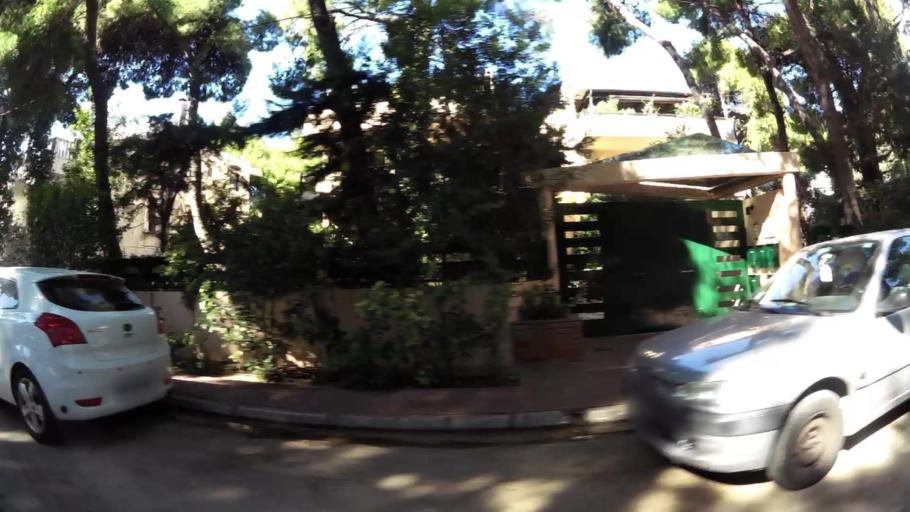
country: GR
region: Attica
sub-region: Nomarchia Athinas
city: Nea Erythraia
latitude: 38.0926
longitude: 23.7970
